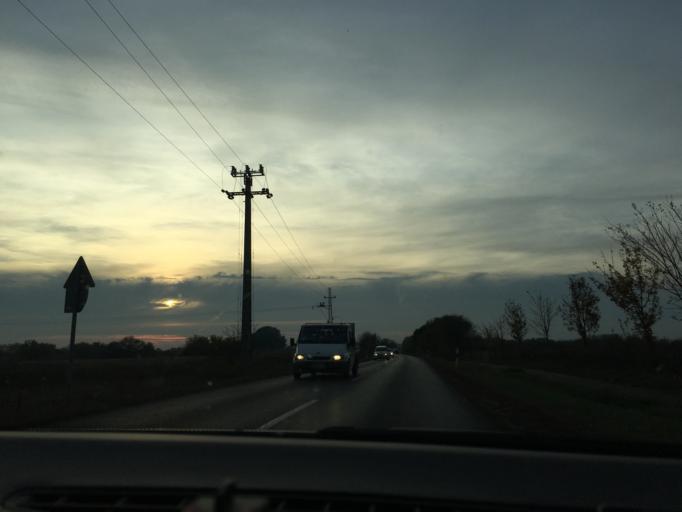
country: HU
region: Szabolcs-Szatmar-Bereg
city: Kallosemjen
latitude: 47.8601
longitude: 21.9034
